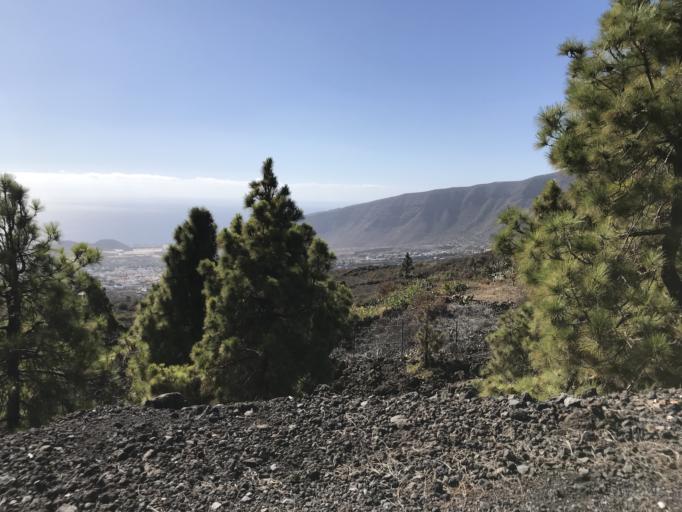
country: ES
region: Canary Islands
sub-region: Provincia de Santa Cruz de Tenerife
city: Arafo
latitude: 28.3271
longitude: -16.4297
